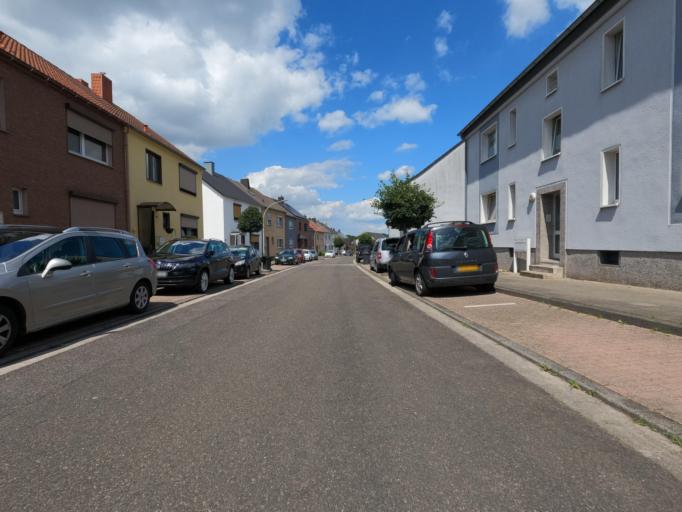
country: DE
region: North Rhine-Westphalia
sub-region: Regierungsbezirk Koln
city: Ubach-Palenberg
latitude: 50.9422
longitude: 6.1109
